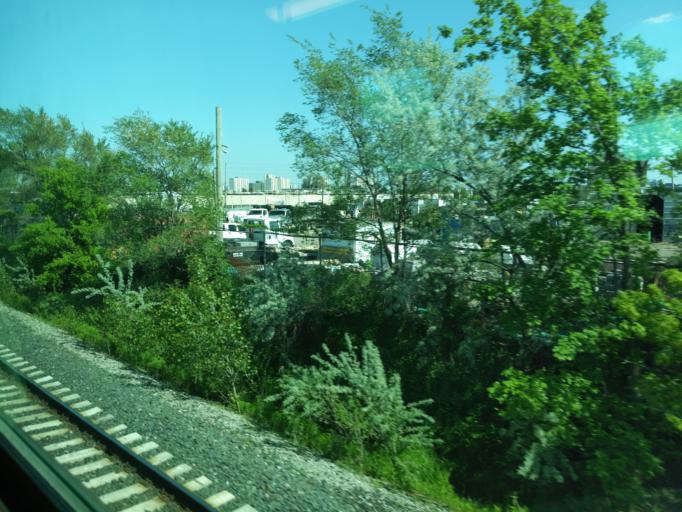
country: CA
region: Ontario
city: Etobicoke
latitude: 43.7062
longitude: -79.5716
